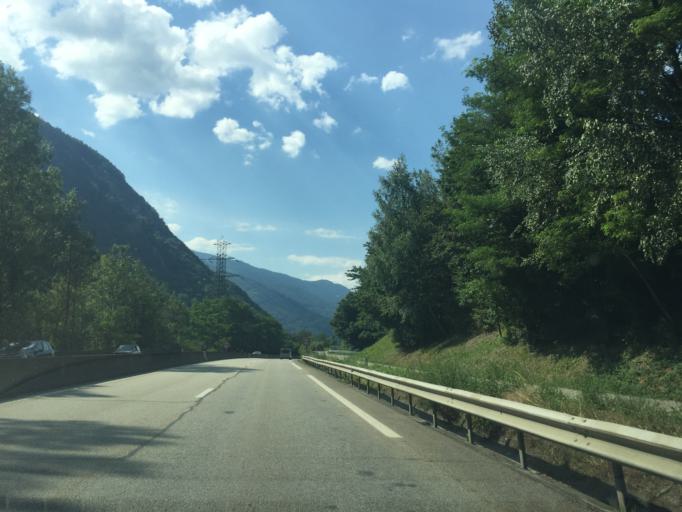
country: FR
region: Rhone-Alpes
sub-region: Departement de la Savoie
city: La Bathie
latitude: 45.5692
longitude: 6.4665
